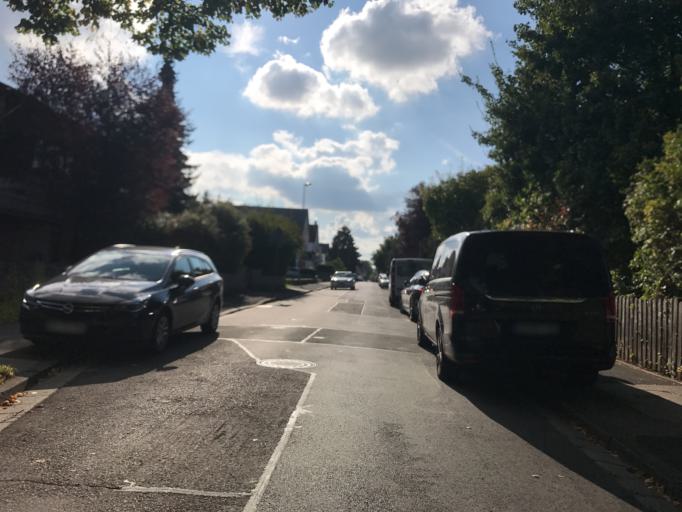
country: DE
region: Rheinland-Pfalz
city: Mainz
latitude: 49.9808
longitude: 8.2504
